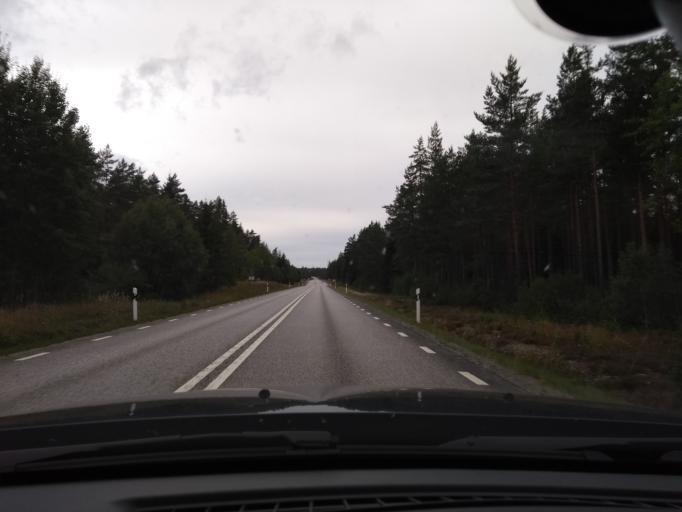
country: SE
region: OEstergoetland
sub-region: Ydre Kommun
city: OEsterbymo
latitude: 57.6434
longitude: 15.1832
